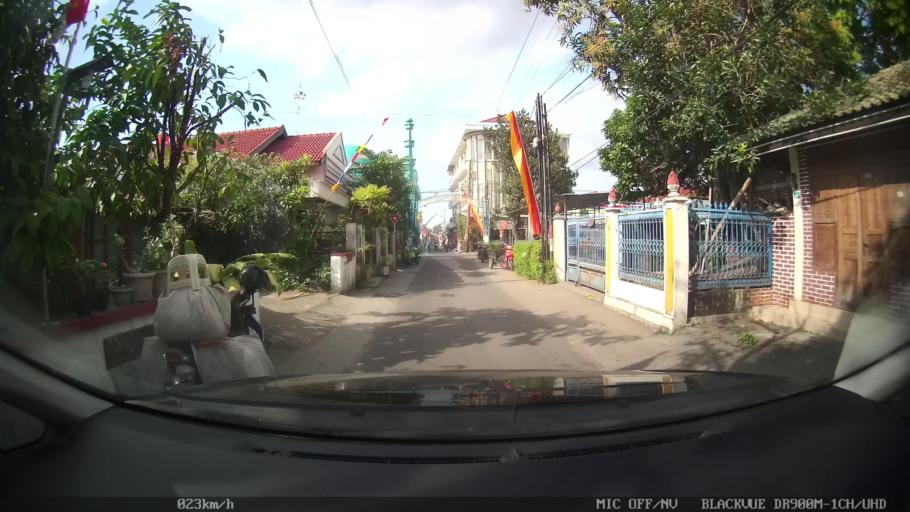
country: ID
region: Daerah Istimewa Yogyakarta
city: Kasihan
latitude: -7.8236
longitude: 110.3644
